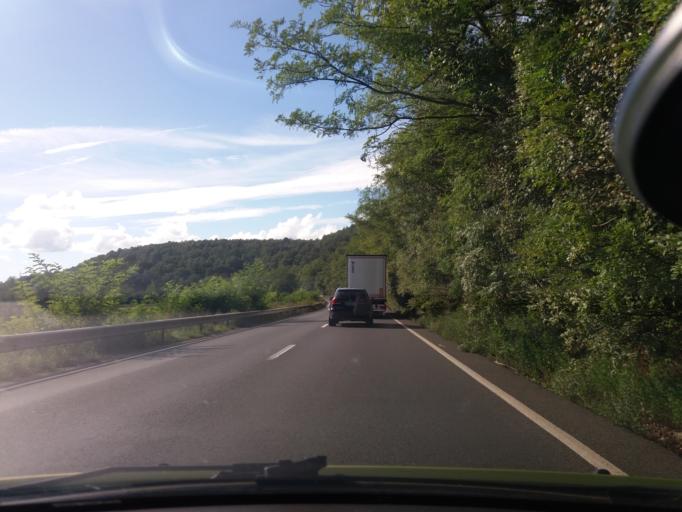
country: RO
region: Arad
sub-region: Comuna Bata
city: Bata
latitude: 46.0362
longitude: 22.0816
